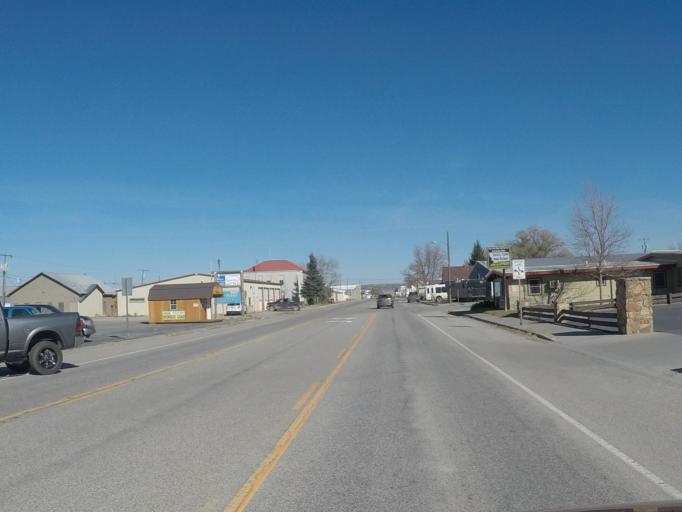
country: US
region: Montana
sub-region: Sweet Grass County
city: Big Timber
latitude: 45.8331
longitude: -109.9583
